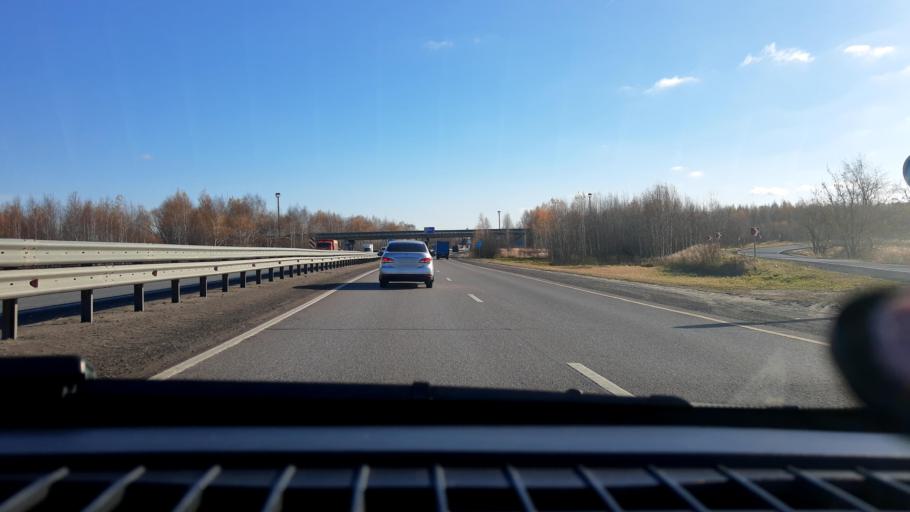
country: RU
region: Nizjnij Novgorod
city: Afonino
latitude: 56.1959
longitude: 44.1186
